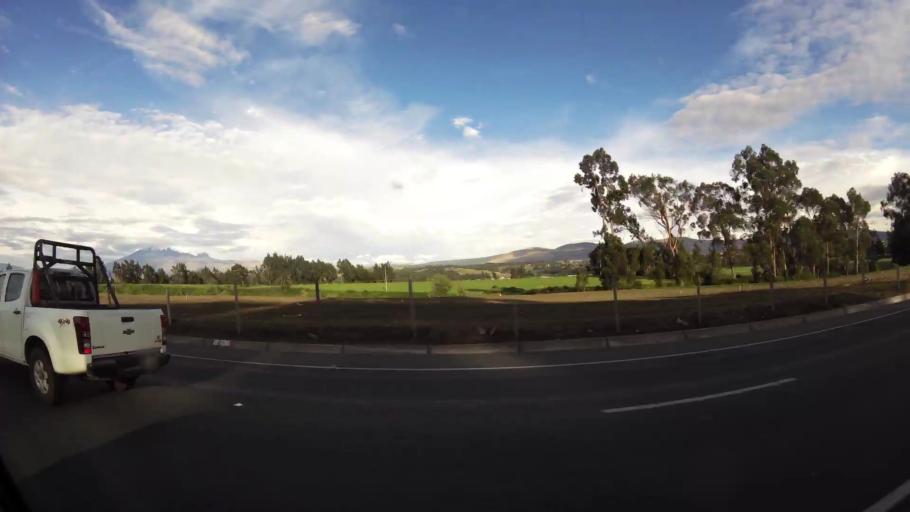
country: EC
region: Cotopaxi
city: Saquisili
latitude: -0.8346
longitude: -78.6191
